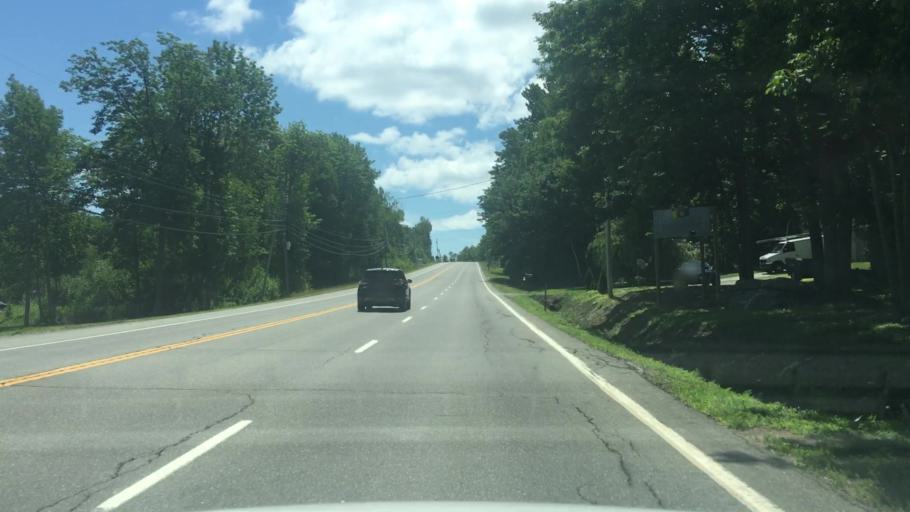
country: US
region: Maine
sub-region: Waldo County
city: Northport
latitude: 44.3651
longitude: -68.9786
